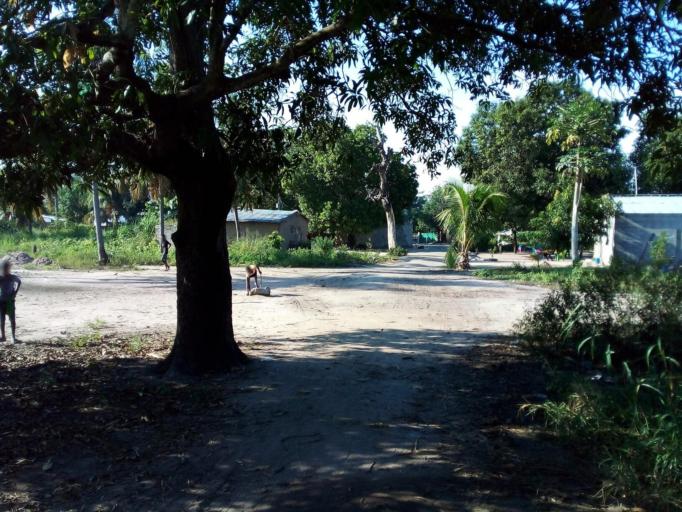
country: MZ
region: Zambezia
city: Quelimane
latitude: -17.5977
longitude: 36.8065
